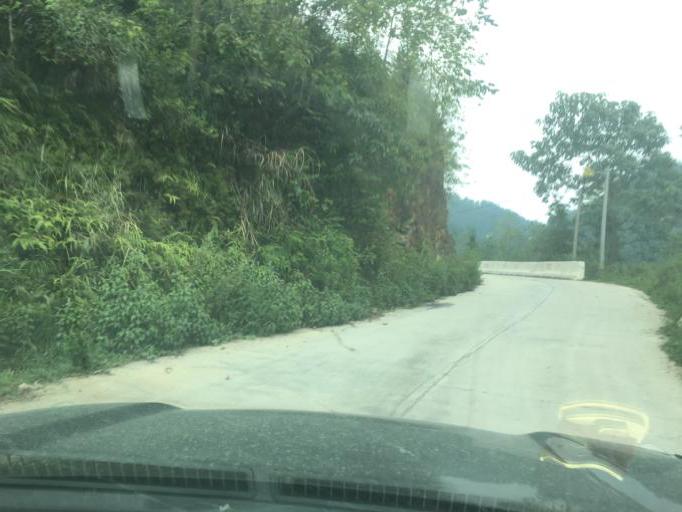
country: CN
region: Guangxi Zhuangzu Zizhiqu
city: Tongle
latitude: 25.3863
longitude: 106.2667
